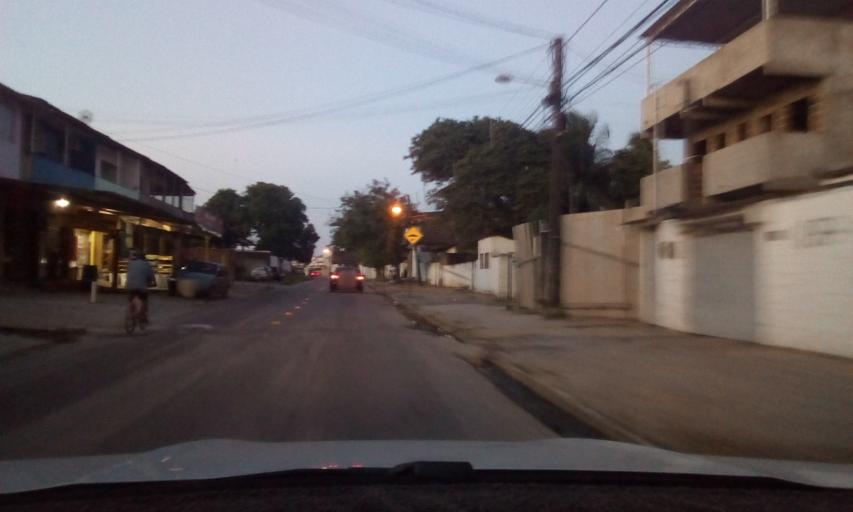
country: BR
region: Paraiba
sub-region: Bayeux
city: Bayeux
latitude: -7.1630
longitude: -34.9064
